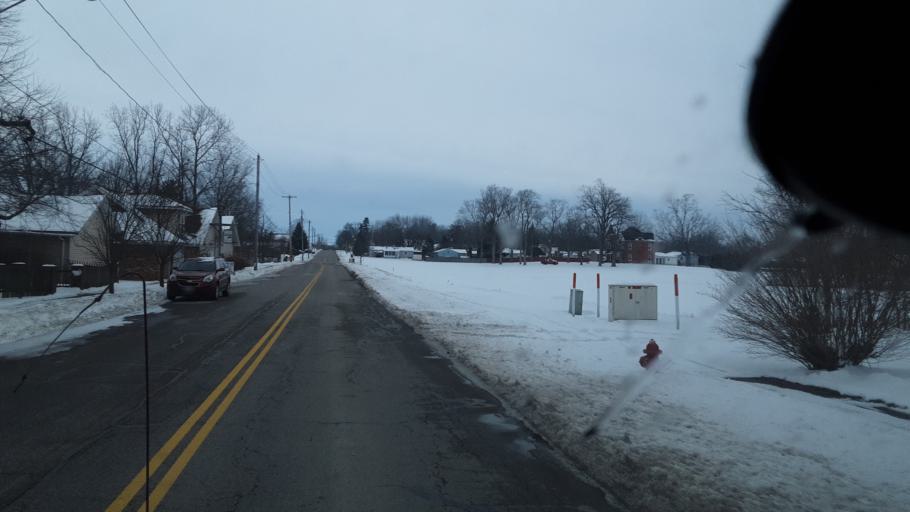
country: US
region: Ohio
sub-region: Madison County
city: London
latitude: 39.8799
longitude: -83.4501
